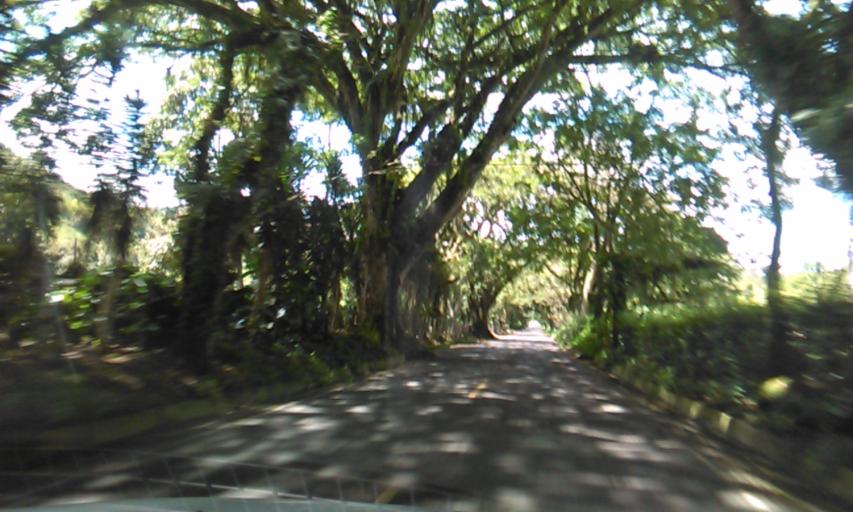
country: CO
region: Quindio
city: Cordoba
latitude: 4.4046
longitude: -75.7084
